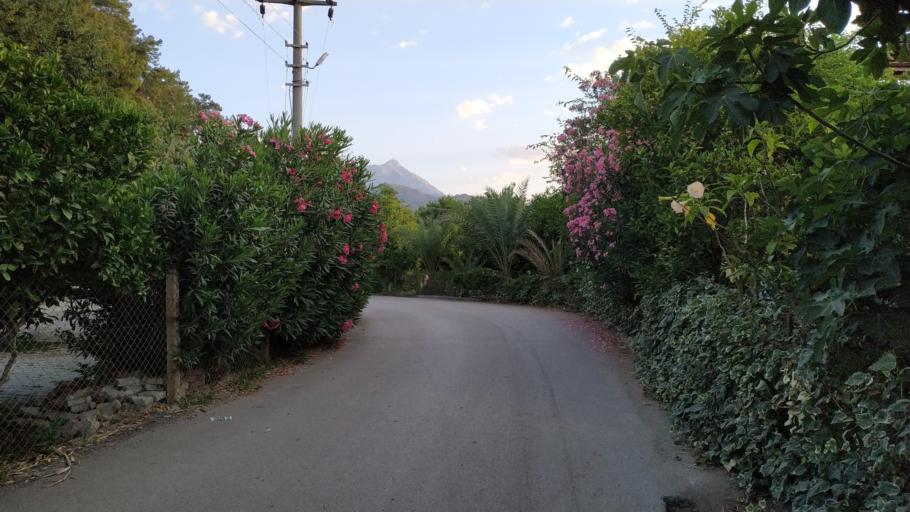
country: TR
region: Antalya
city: Tekirova
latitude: 36.4088
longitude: 30.4748
